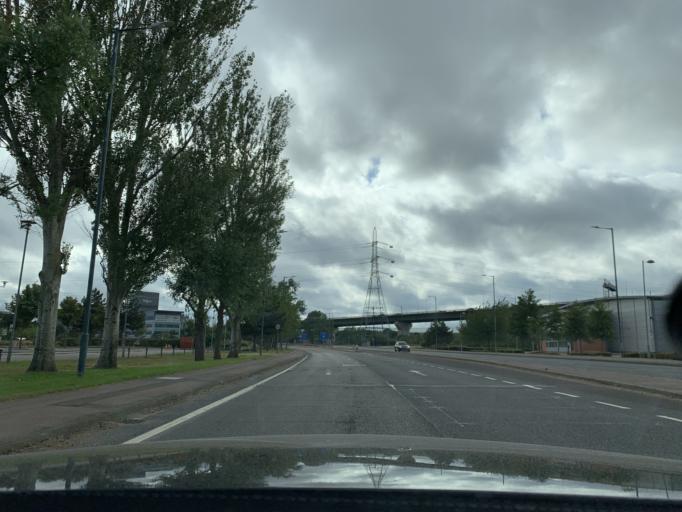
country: GB
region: England
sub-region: Kent
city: Stone
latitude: 51.4563
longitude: 0.2539
